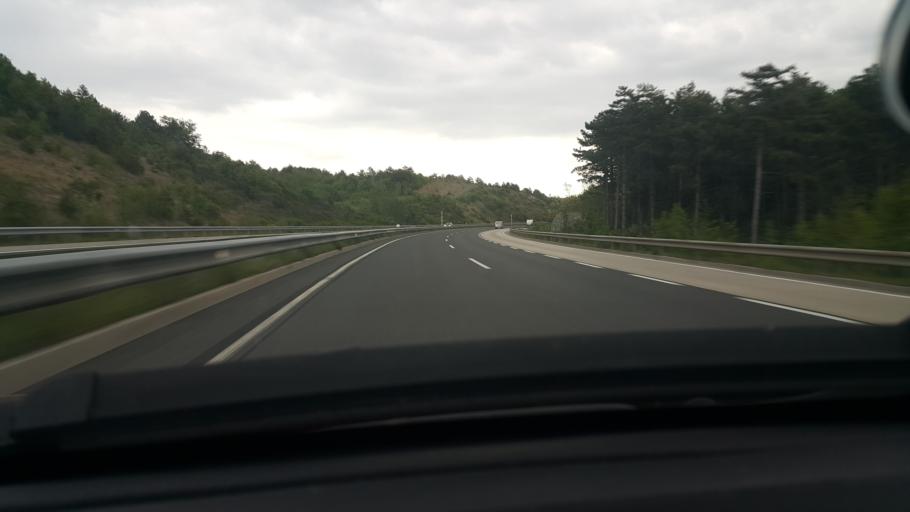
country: SI
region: Koper-Capodistria
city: Dekani
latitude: 45.5565
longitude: 13.8439
